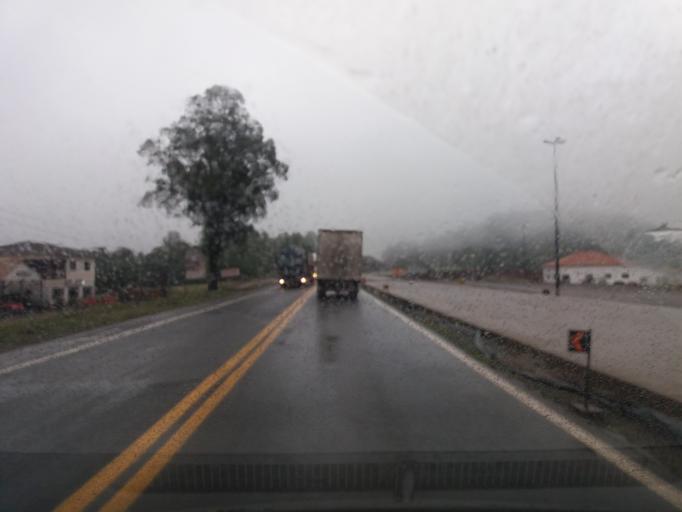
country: BR
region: Parana
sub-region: Realeza
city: Realeza
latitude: -25.4606
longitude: -53.5826
